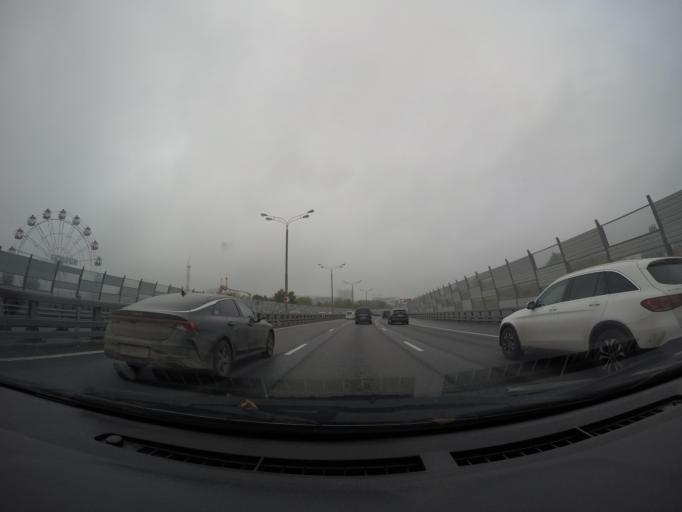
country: RU
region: Moscow
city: Shchukino
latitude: 55.7729
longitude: 37.4347
